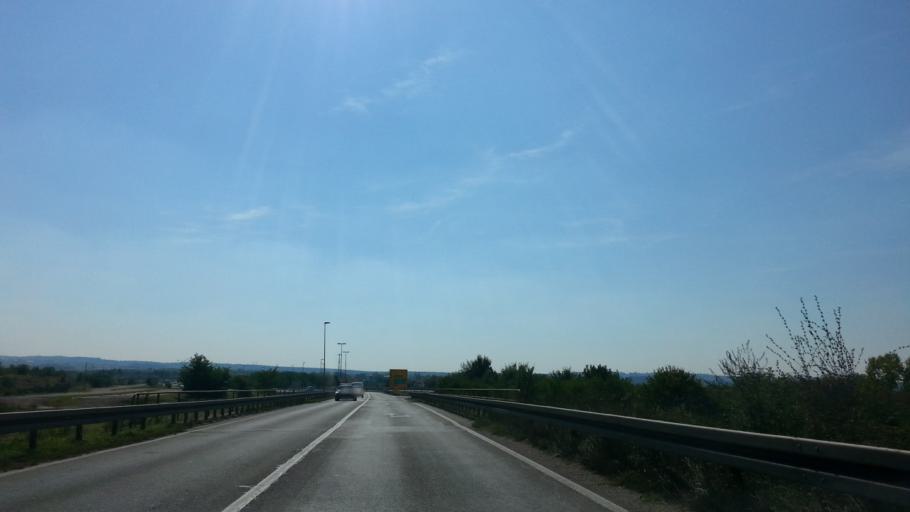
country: RS
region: Central Serbia
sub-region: Belgrade
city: Rakovica
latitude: 44.7193
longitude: 20.4159
